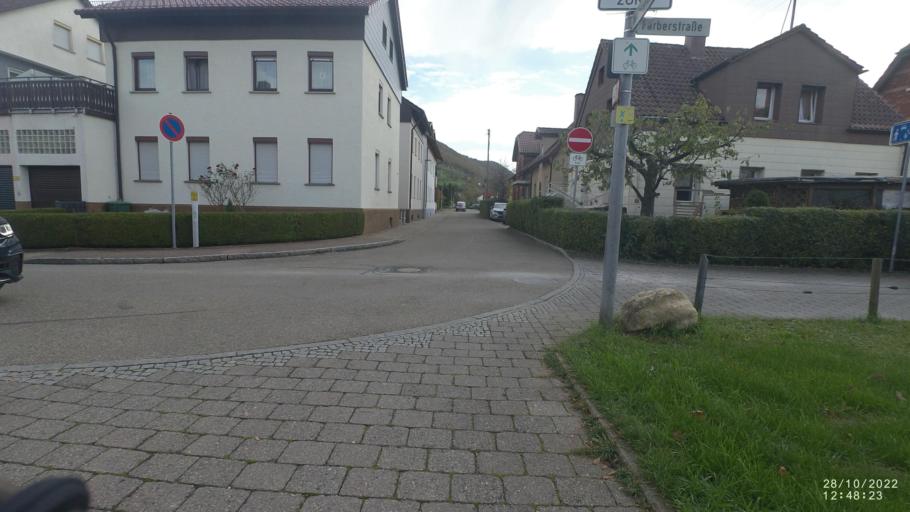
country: DE
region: Baden-Wuerttemberg
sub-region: Regierungsbezirk Stuttgart
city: Kuchen
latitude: 48.6454
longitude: 9.7938
